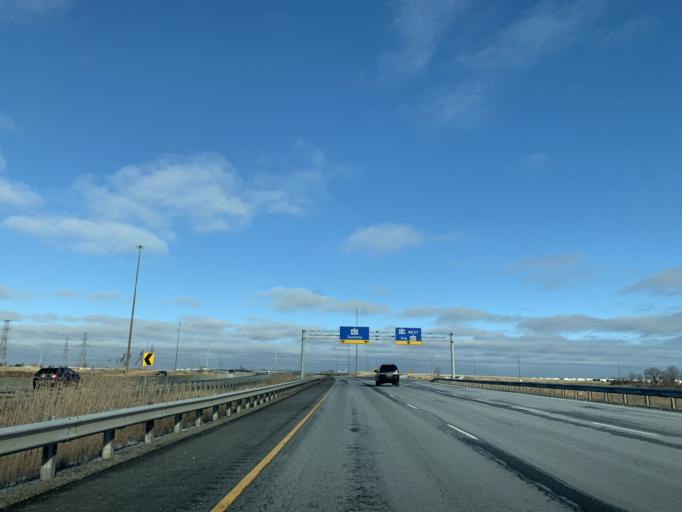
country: CA
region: Ontario
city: Oakville
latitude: 43.5215
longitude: -79.7325
